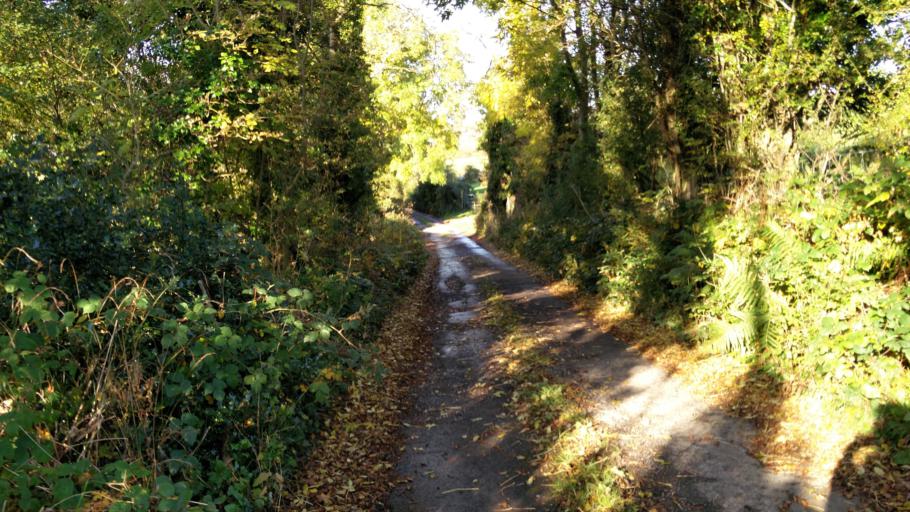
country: IE
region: Connaught
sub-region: Maigh Eo
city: Westport
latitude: 53.7831
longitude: -9.4583
